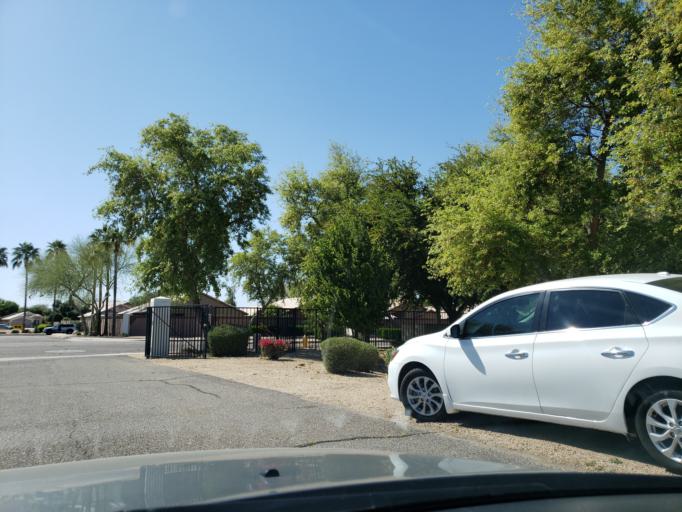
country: US
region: Arizona
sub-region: Maricopa County
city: Glendale
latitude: 33.5517
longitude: -112.1728
